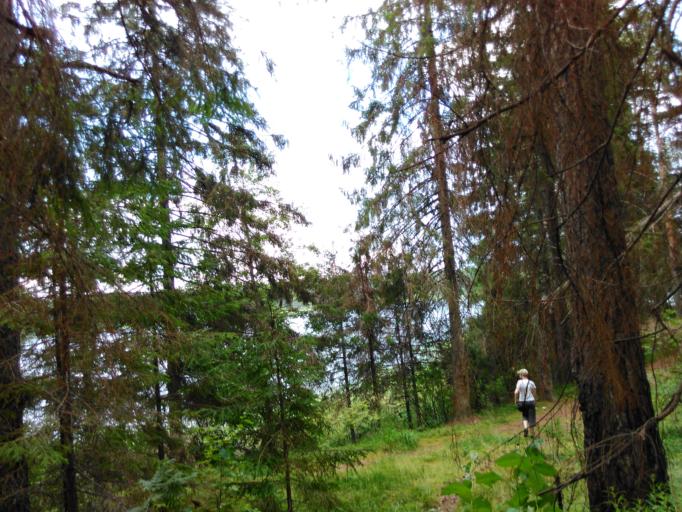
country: RU
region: Tverskaya
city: Ostashkov
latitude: 57.2436
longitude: 33.0132
